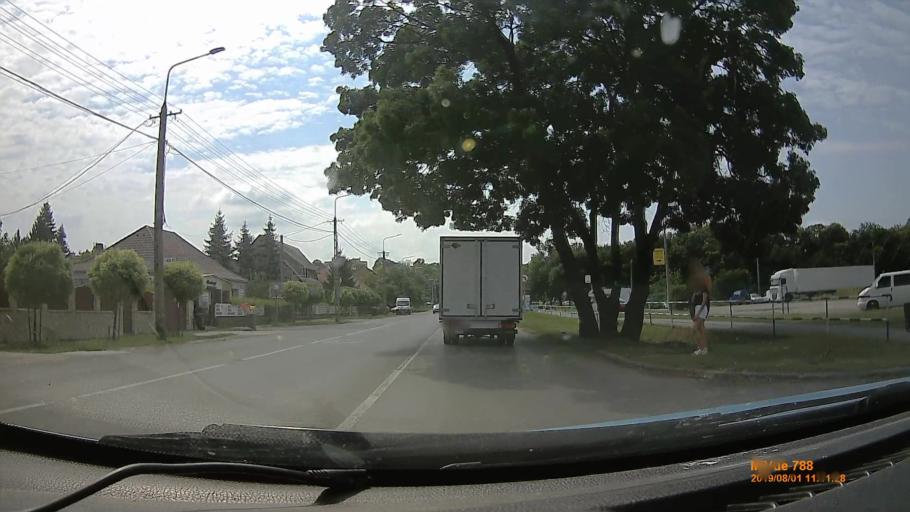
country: HU
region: Baranya
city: Pecs
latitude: 46.0491
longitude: 18.2136
